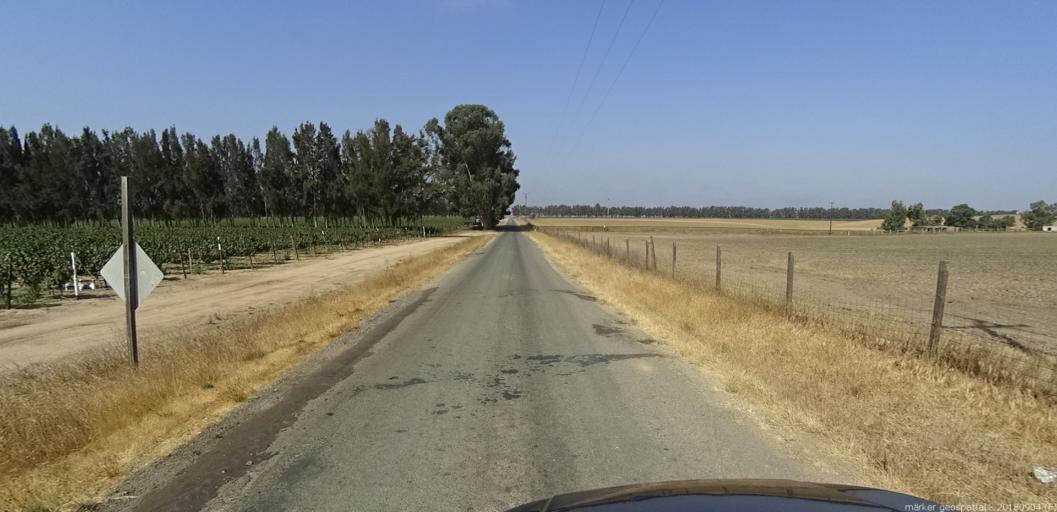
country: US
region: California
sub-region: Monterey County
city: Soledad
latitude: 36.4815
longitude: -121.3514
